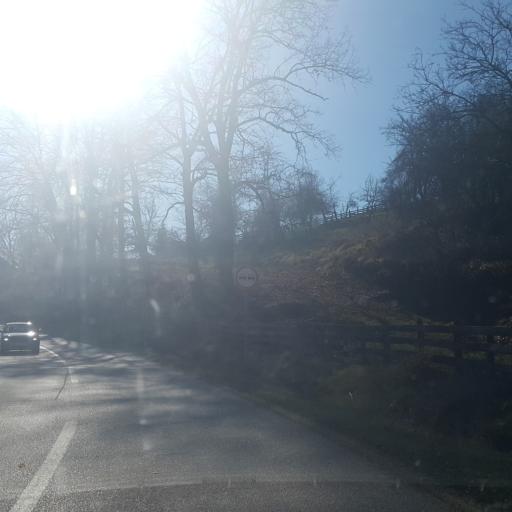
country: RS
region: Central Serbia
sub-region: Sumadijski Okrug
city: Raca
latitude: 44.2455
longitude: 20.8886
